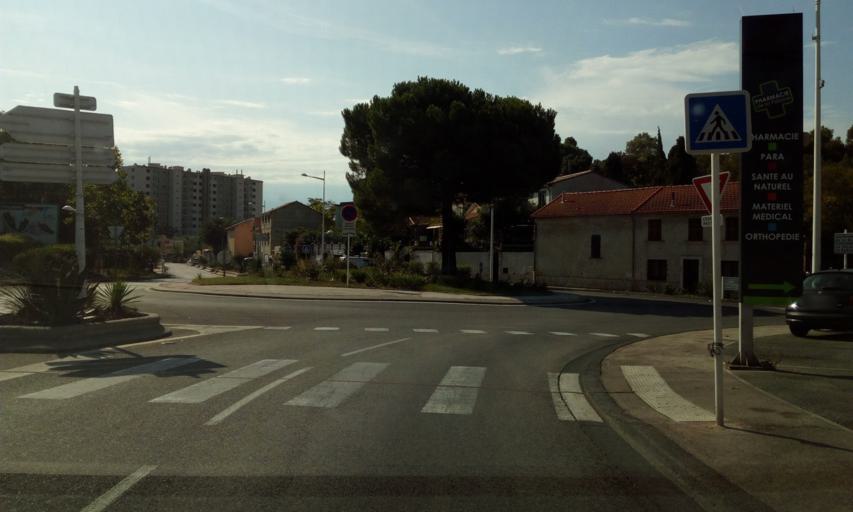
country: FR
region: Provence-Alpes-Cote d'Azur
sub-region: Departement du Var
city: La Valette-du-Var
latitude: 43.1241
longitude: 5.9699
